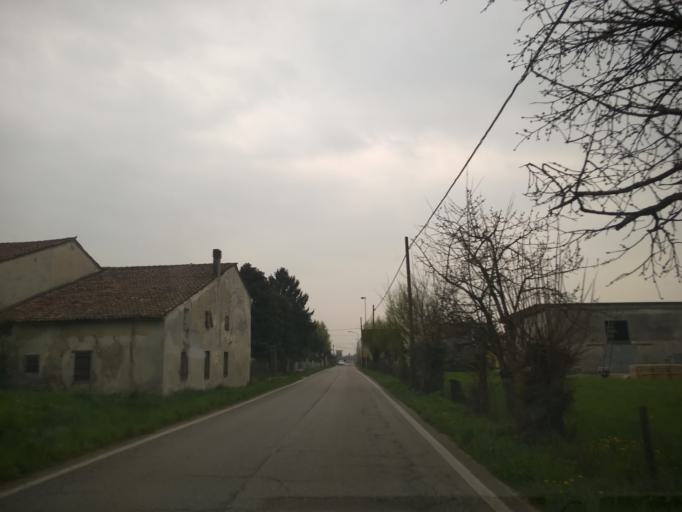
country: IT
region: Veneto
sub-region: Provincia di Vicenza
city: Pozzoleone
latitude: 45.6318
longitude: 11.6582
